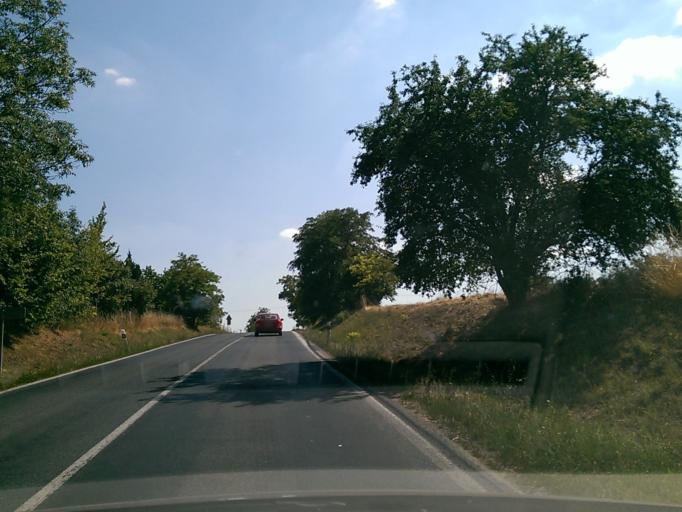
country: CZ
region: South Moravian
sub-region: Okres Breclav
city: Mikulov
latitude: 48.7902
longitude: 16.6757
